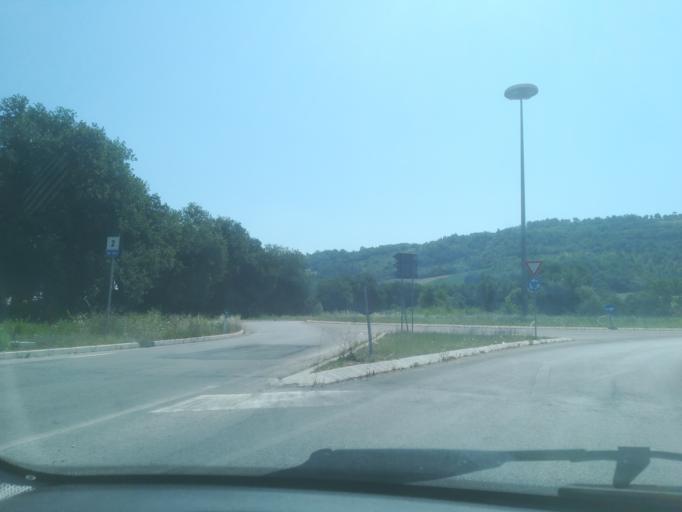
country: IT
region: The Marches
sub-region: Provincia di Macerata
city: Villa Potenza
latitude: 43.3333
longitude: 13.4383
